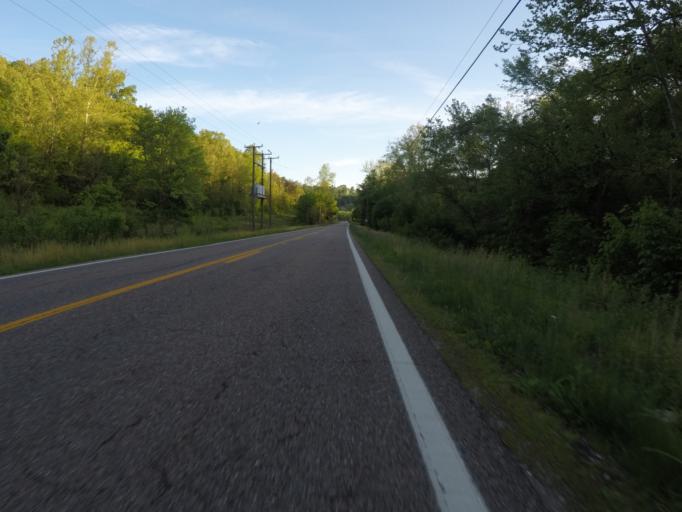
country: US
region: West Virginia
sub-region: Cabell County
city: Huntington
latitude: 38.4986
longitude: -82.4755
